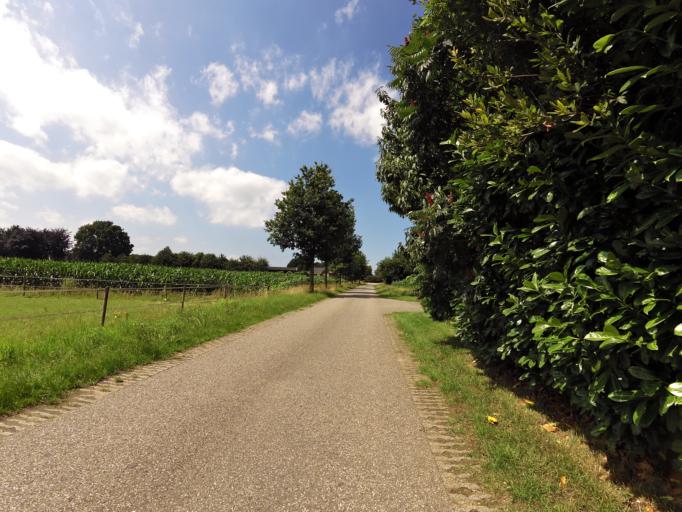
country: NL
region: Gelderland
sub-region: Gemeente Doesburg
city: Doesburg
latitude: 51.9626
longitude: 6.1617
